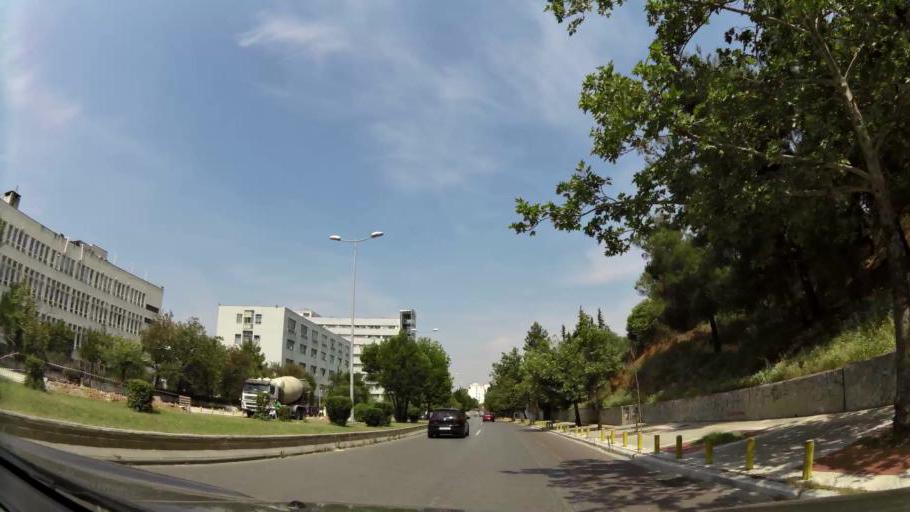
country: GR
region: Central Macedonia
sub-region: Nomos Thessalonikis
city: Agios Pavlos
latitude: 40.6330
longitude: 22.9592
